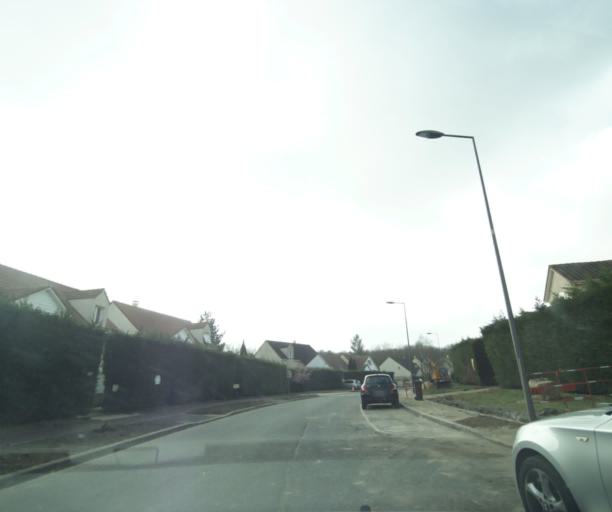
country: FR
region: Ile-de-France
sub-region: Departement du Val-d'Oise
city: Vaureal
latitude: 49.0401
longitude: 2.0226
